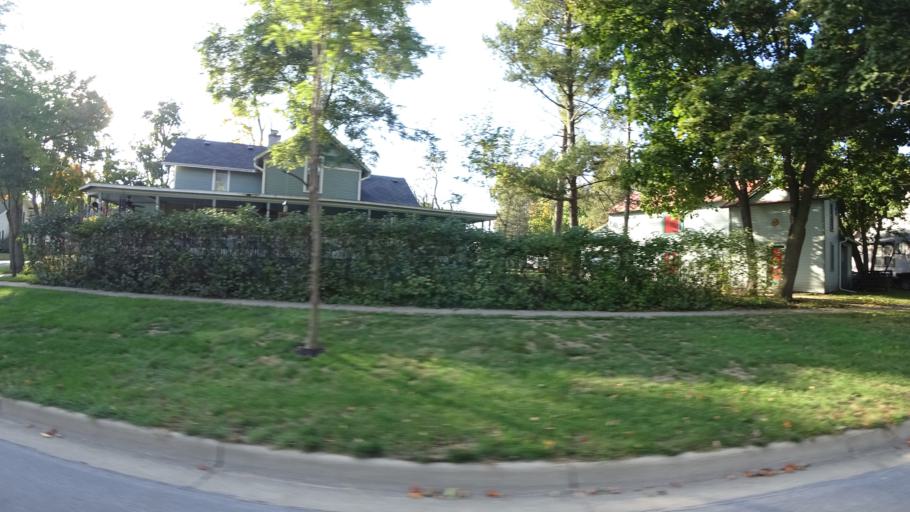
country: US
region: Michigan
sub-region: Saint Joseph County
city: Three Rivers
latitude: 41.9514
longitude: -85.6303
